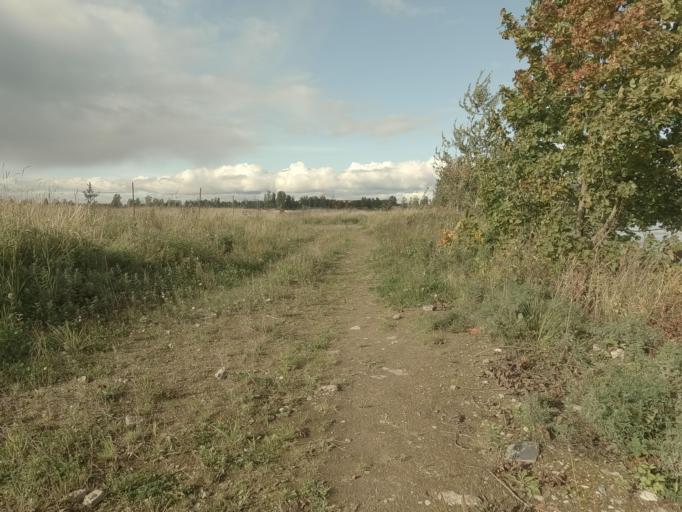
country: RU
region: St.-Petersburg
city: Krasnogvargeisky
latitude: 59.9768
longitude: 30.4903
